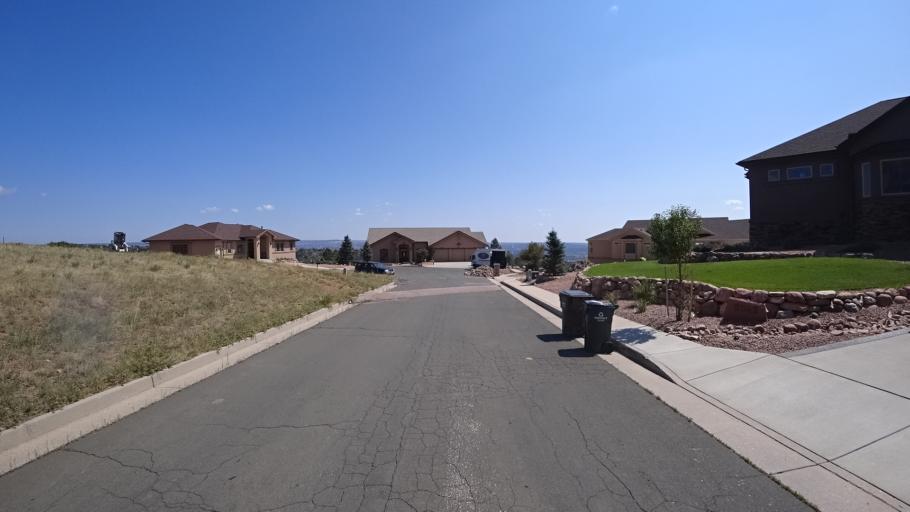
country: US
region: Colorado
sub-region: El Paso County
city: Air Force Academy
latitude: 38.9255
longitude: -104.8767
